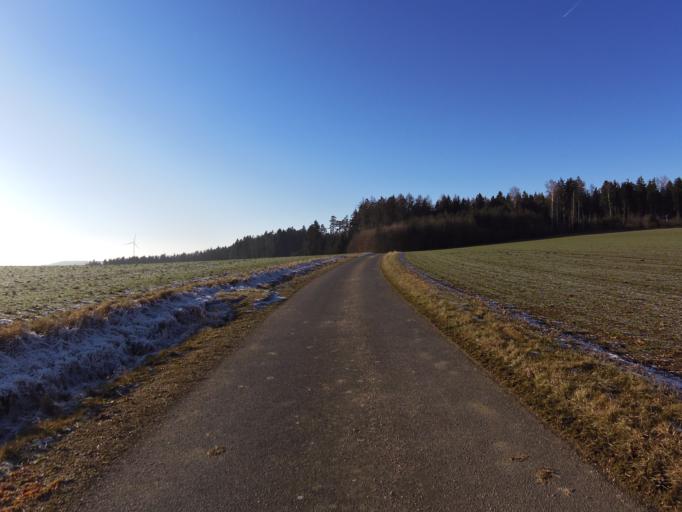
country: DE
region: Bavaria
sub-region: Upper Franconia
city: Hochstadt bei Thiersheim
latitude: 50.0686
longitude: 12.0482
